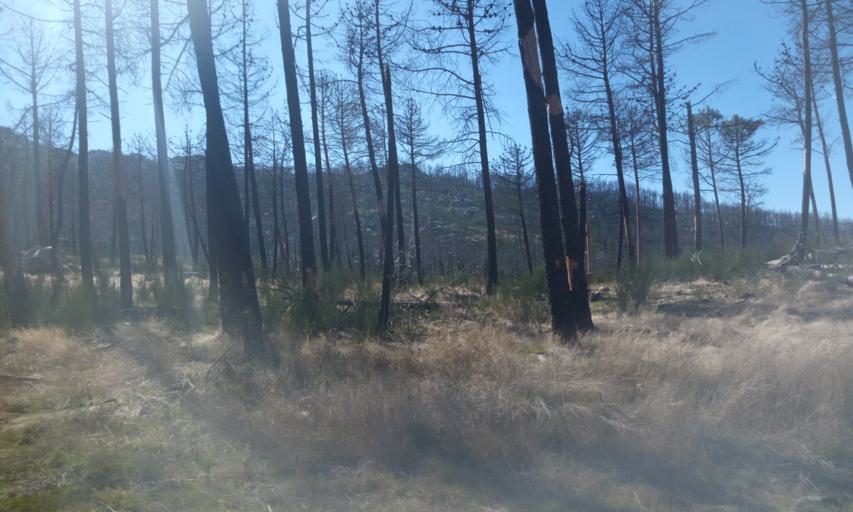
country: PT
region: Guarda
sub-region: Manteigas
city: Manteigas
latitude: 40.4924
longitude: -7.5223
